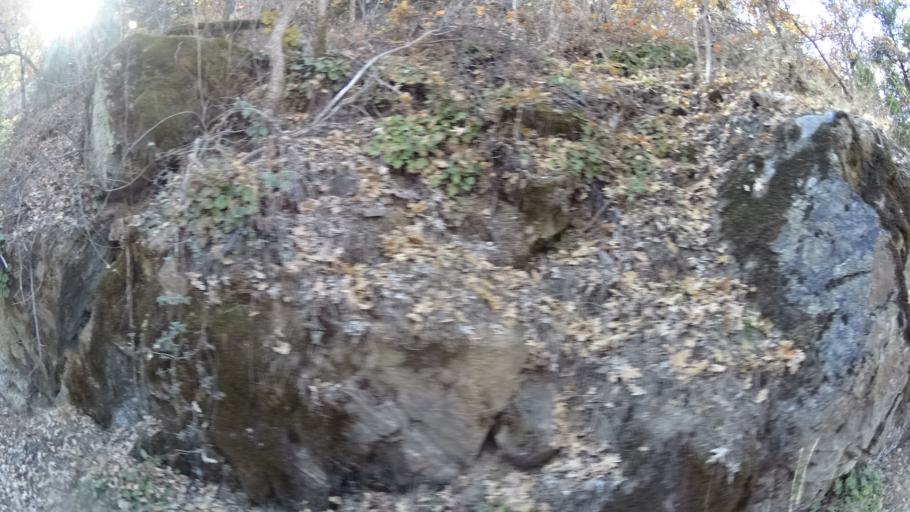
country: US
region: California
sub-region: Siskiyou County
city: Yreka
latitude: 41.8608
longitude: -122.7821
